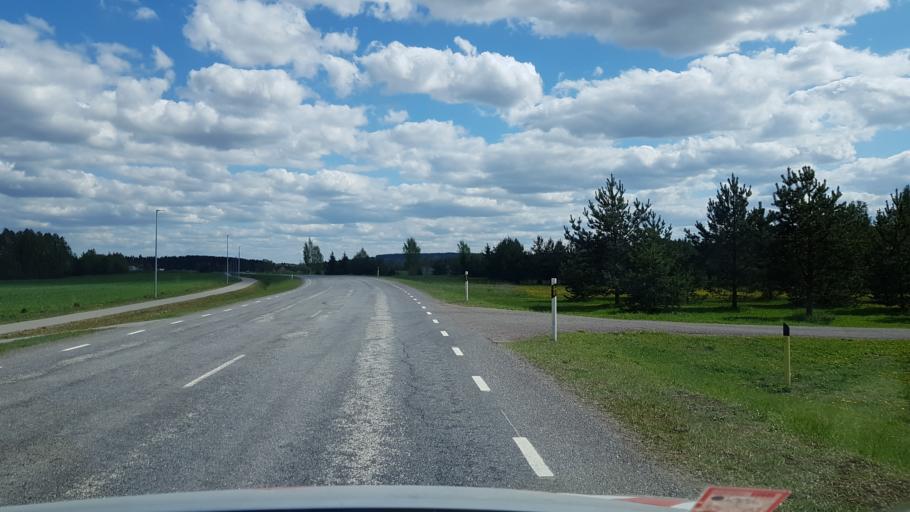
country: EE
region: Tartu
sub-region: UElenurme vald
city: Ulenurme
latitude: 58.3103
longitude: 26.8473
